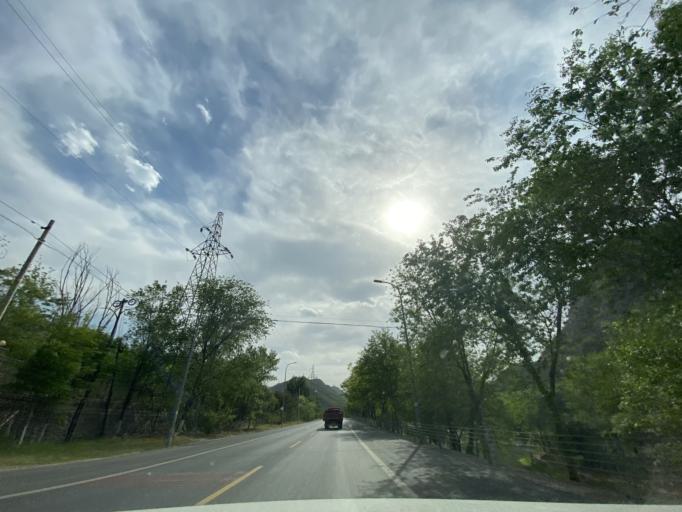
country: CN
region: Beijing
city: Miaofengshan
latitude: 39.9879
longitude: 116.0641
